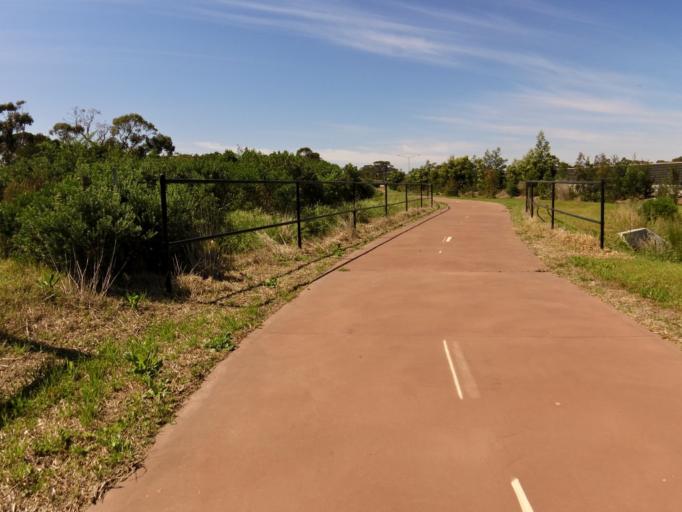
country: AU
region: Victoria
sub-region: Greater Dandenong
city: Springvale South
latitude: -37.9635
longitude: 145.1319
